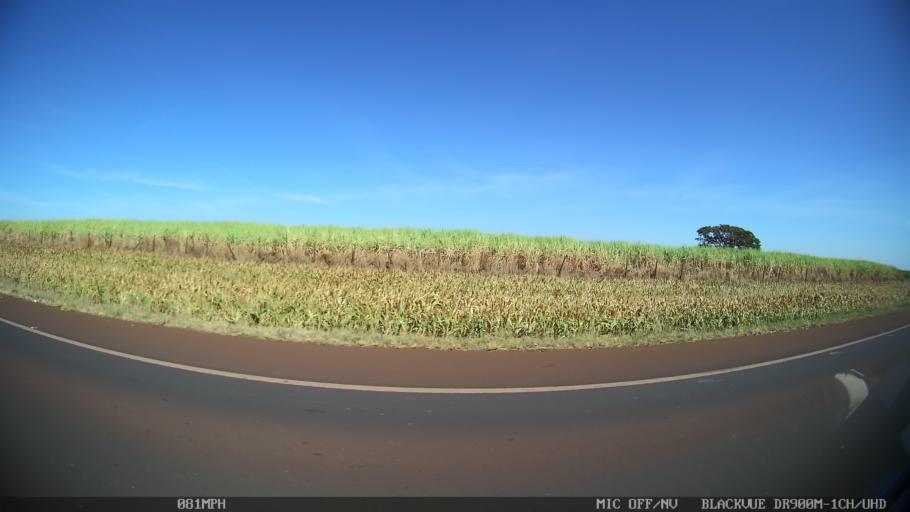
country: BR
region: Sao Paulo
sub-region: Ipua
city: Ipua
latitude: -20.4678
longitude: -48.1200
